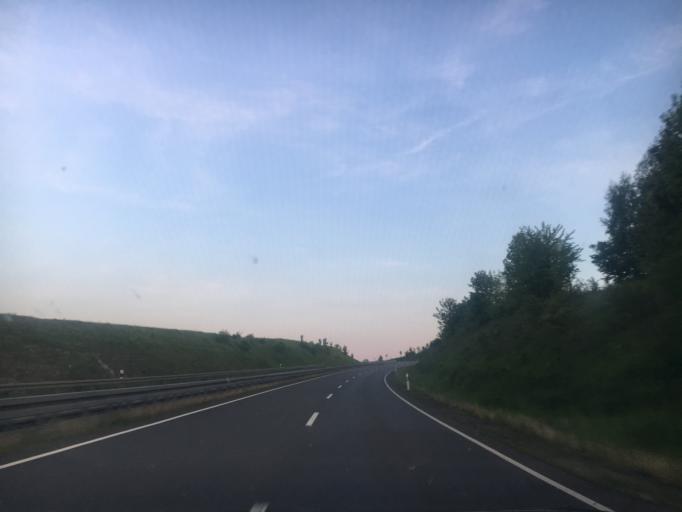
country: DE
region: Thuringia
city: Gera
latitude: 50.8866
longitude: 12.1134
